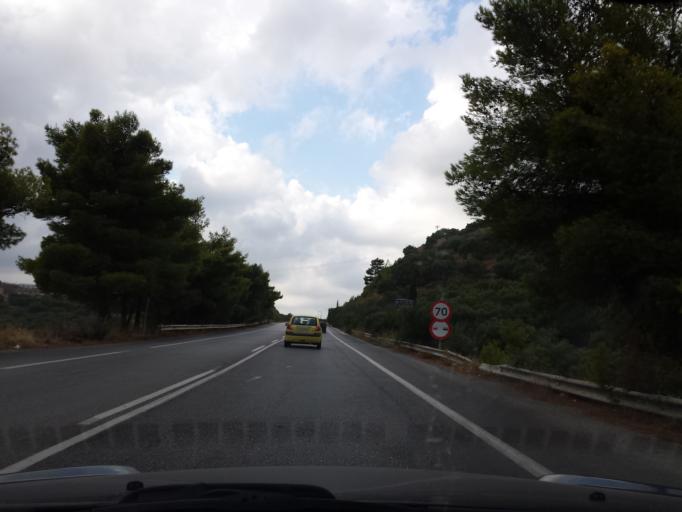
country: GR
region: Crete
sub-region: Nomos Lasithiou
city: Neapoli
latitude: 35.2570
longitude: 25.6156
